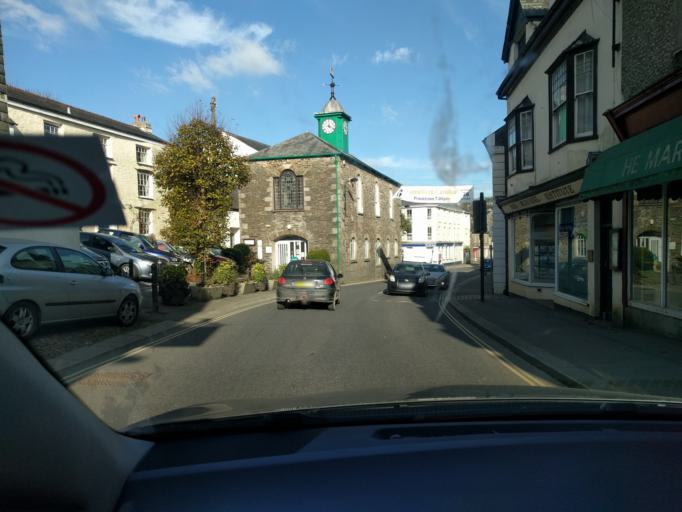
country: GB
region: England
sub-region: Cornwall
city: Camelford
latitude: 50.6222
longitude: -4.6795
